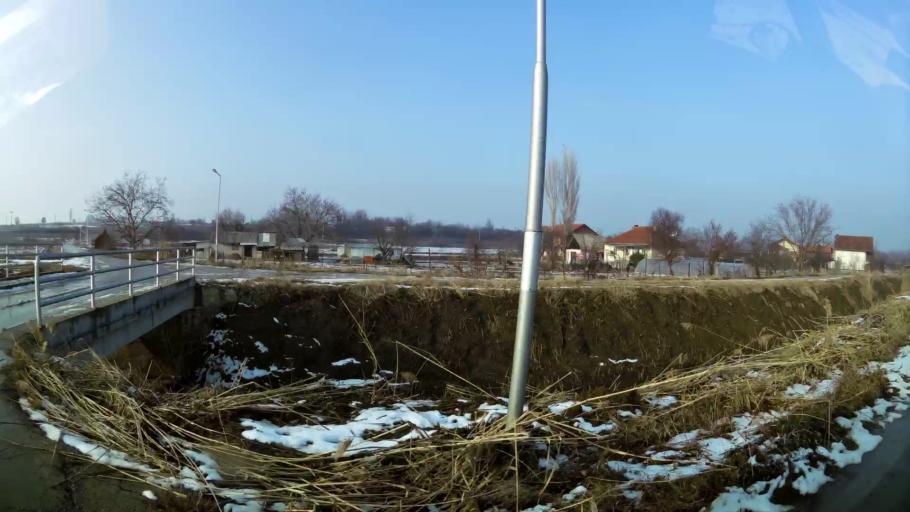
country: MK
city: Miladinovci
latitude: 41.9739
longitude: 21.6432
